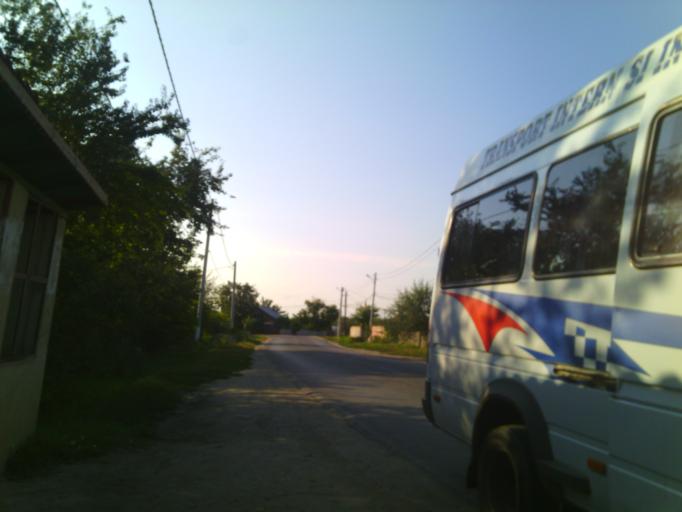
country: RO
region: Giurgiu
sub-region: Comuna Valea Dragului
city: Valea Dragului
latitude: 44.2050
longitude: 26.2718
